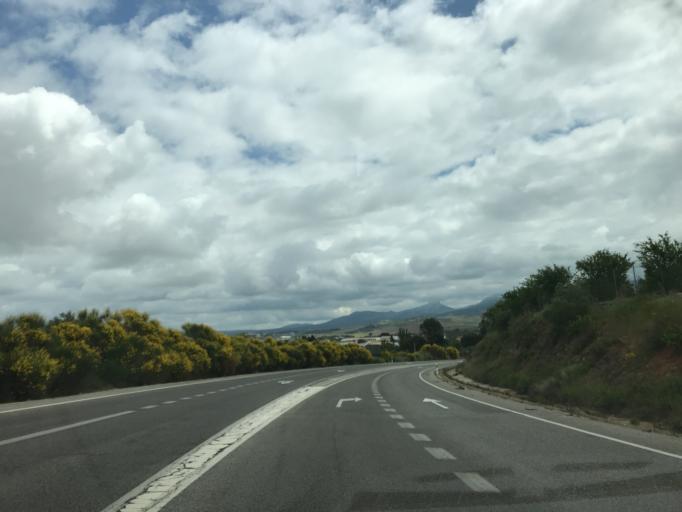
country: ES
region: Andalusia
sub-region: Provincia de Malaga
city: Ronda
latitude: 36.7241
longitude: -5.1707
